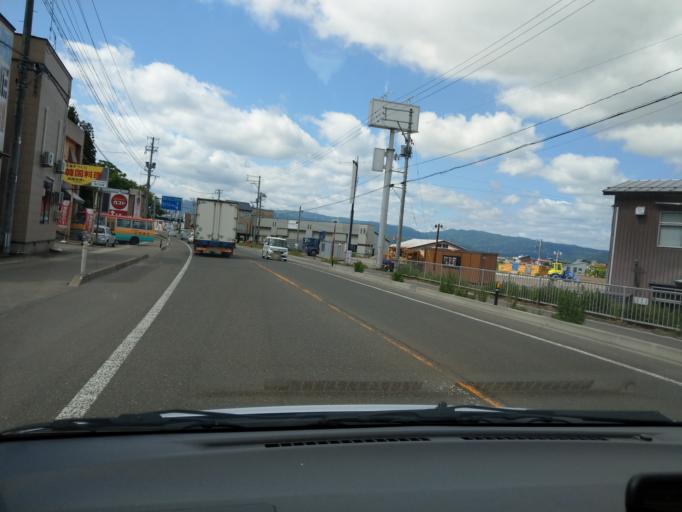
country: JP
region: Akita
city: Yuzawa
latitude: 39.1781
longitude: 140.4933
